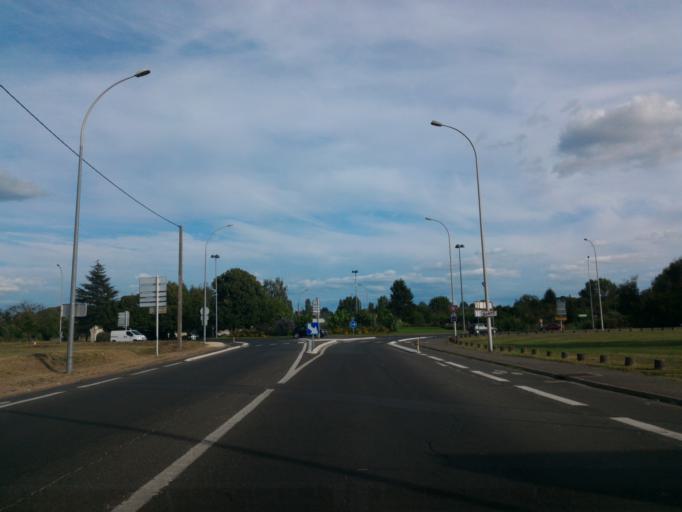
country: FR
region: Centre
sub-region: Departement du Loir-et-Cher
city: Saint-Gervais-la-Foret
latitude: 47.5783
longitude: 1.3476
